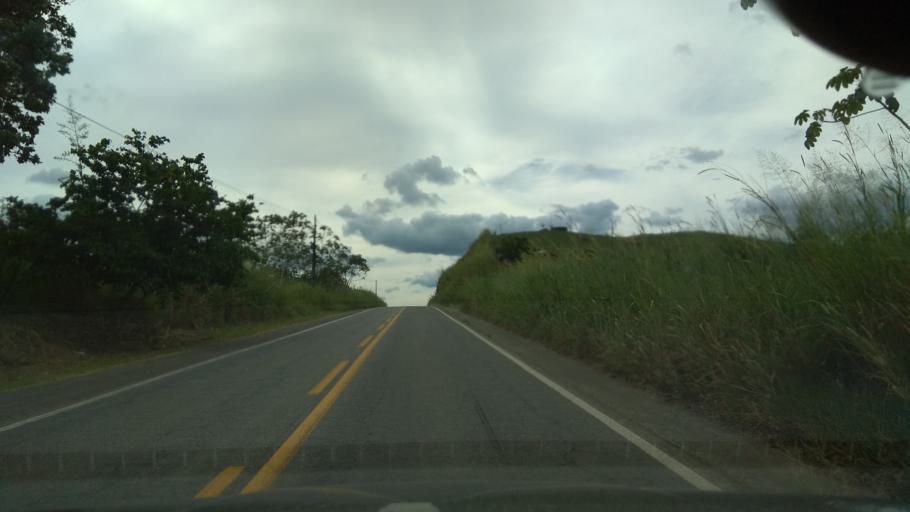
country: BR
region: Bahia
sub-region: Ipiau
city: Ipiau
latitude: -14.1564
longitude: -39.6957
